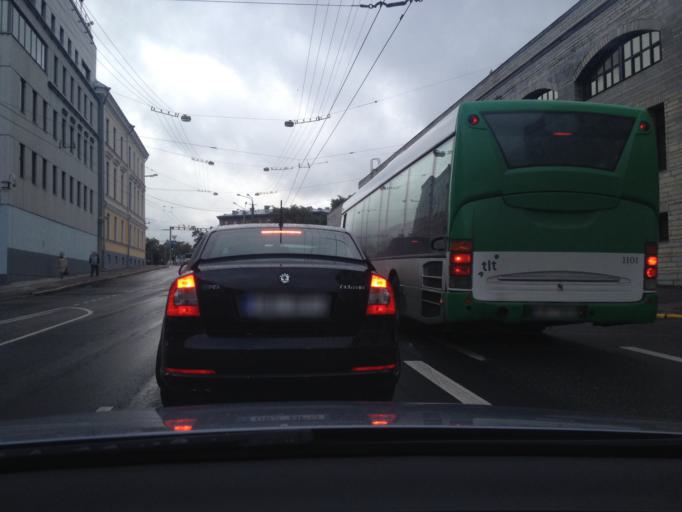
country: EE
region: Harju
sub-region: Tallinna linn
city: Tallinn
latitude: 59.4306
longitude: 24.7373
